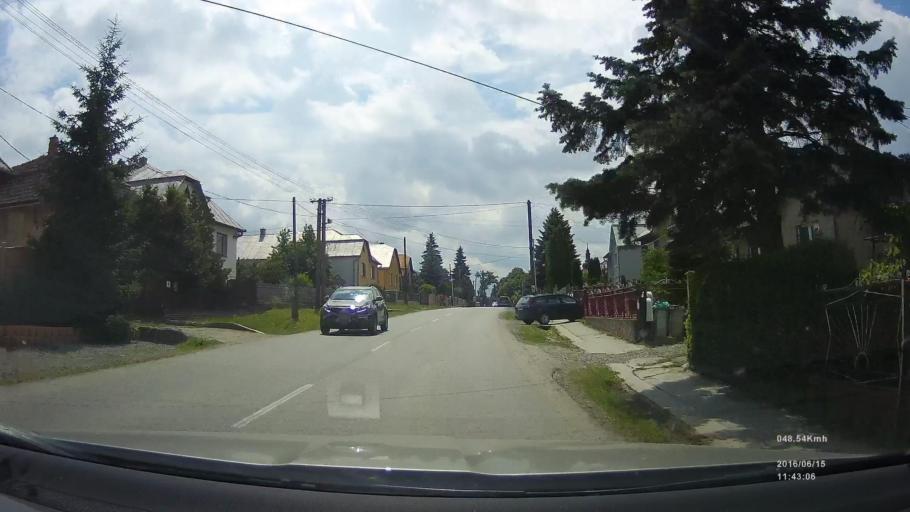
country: SK
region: Kosicky
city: Kosice
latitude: 48.7545
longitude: 21.3430
